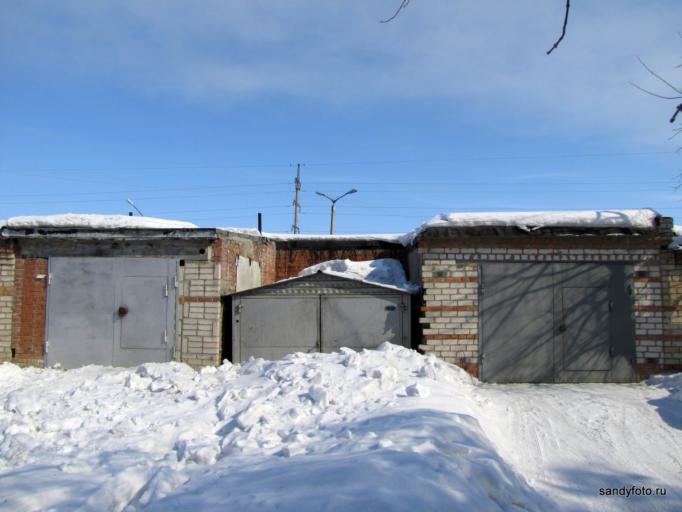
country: RU
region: Chelyabinsk
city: Troitsk
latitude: 54.0920
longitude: 61.5560
